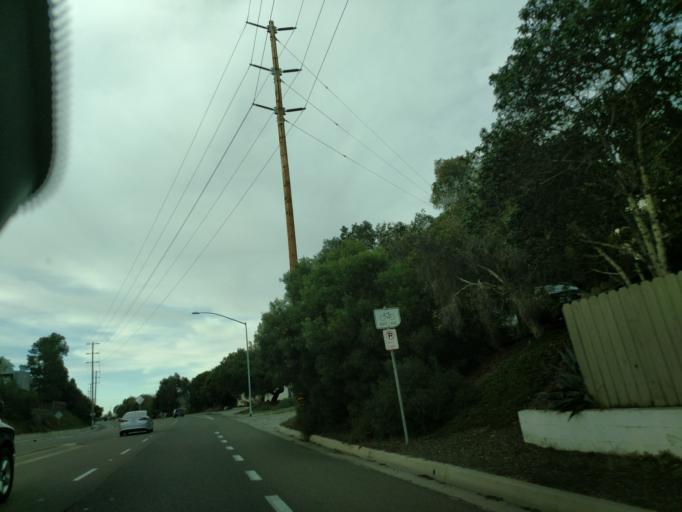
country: US
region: California
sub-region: San Diego County
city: Coronado
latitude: 32.7325
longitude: -117.2283
